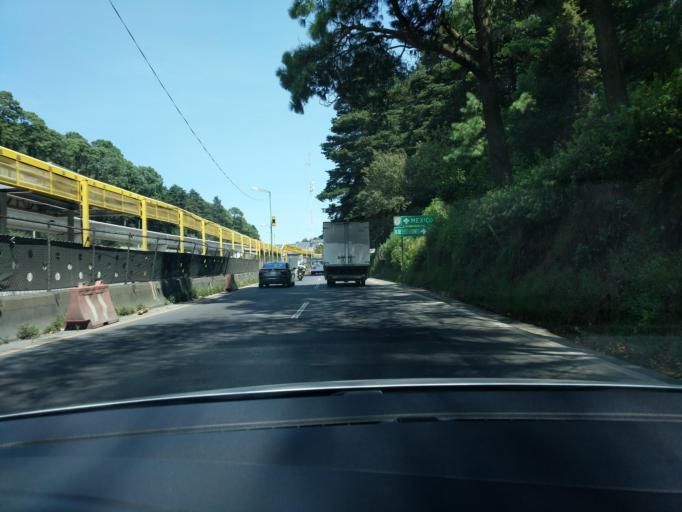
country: MX
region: Mexico City
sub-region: Cuajimalpa de Morelos
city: San Lorenzo Acopilco
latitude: 19.3328
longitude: -99.3137
